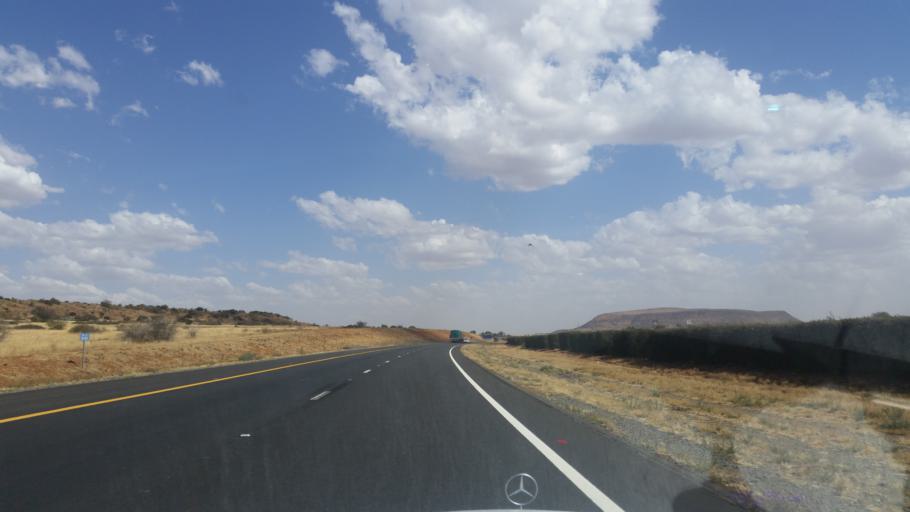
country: ZA
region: Orange Free State
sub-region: Mangaung Metropolitan Municipality
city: Bloemfontein
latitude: -29.1921
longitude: 26.1934
